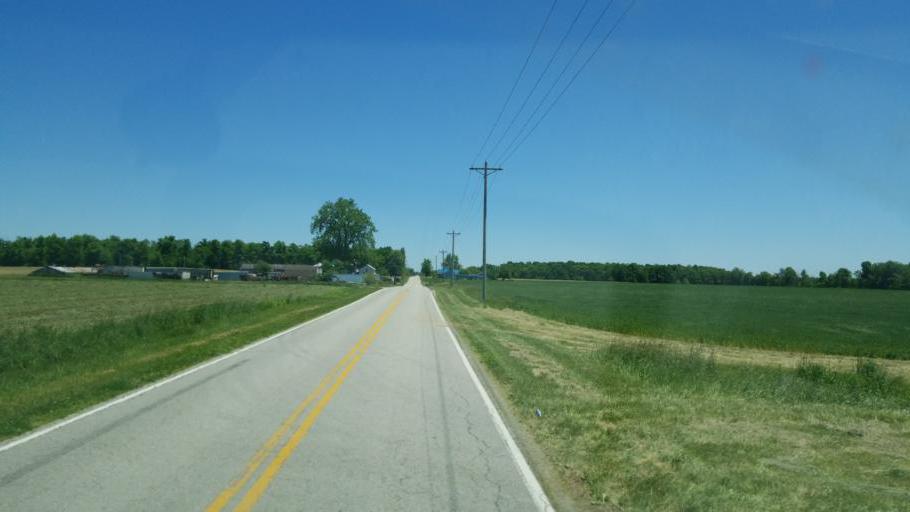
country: US
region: Ohio
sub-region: Darke County
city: Ansonia
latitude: 40.2648
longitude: -84.6575
